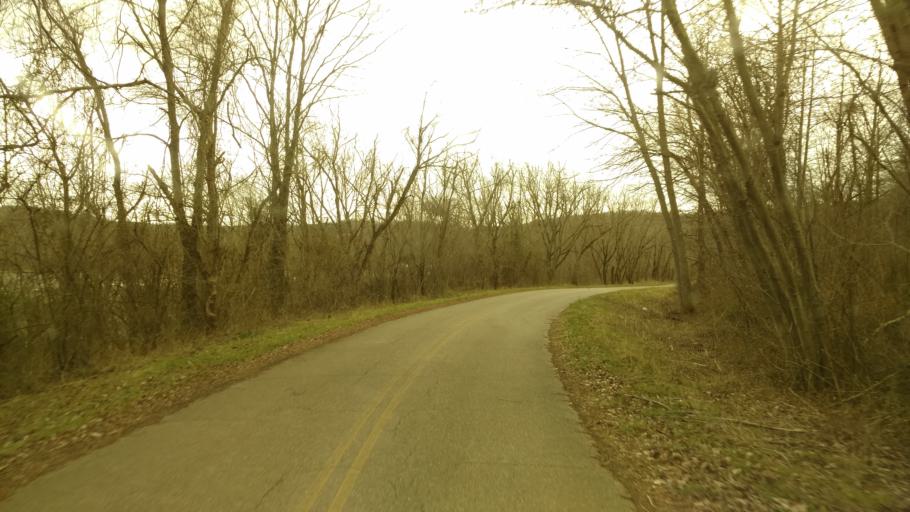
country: US
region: Ohio
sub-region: Muskingum County
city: Frazeysburg
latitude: 40.0288
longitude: -82.1246
